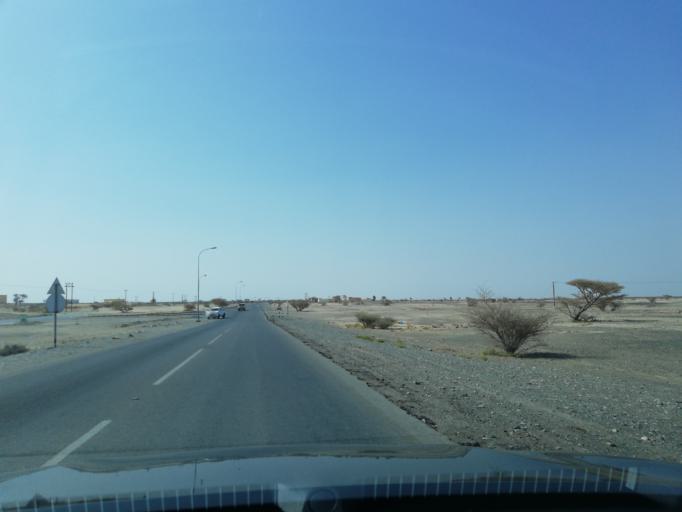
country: OM
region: Muhafazat ad Dakhiliyah
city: Adam
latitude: 22.3656
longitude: 58.0622
